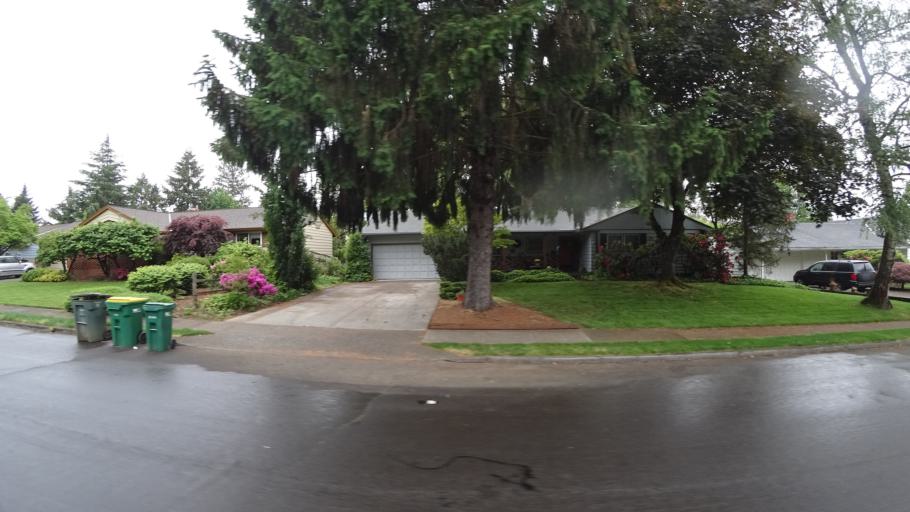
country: US
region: Oregon
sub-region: Washington County
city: Raleigh Hills
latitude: 45.4760
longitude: -122.7727
